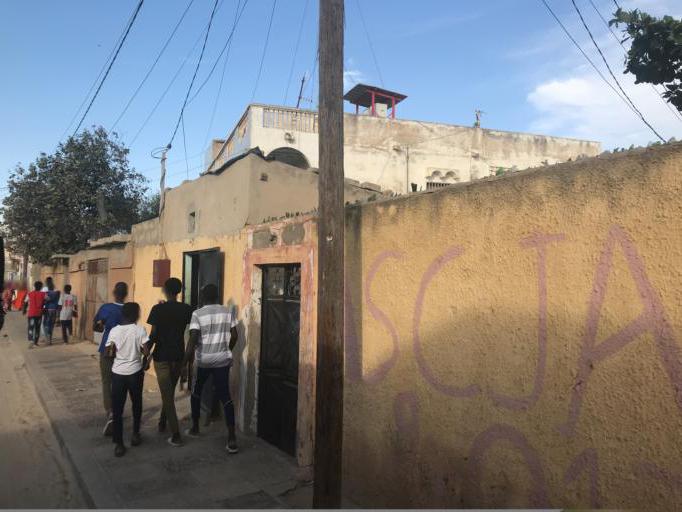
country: SN
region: Saint-Louis
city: Saint-Louis
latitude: 15.9996
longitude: -16.4966
